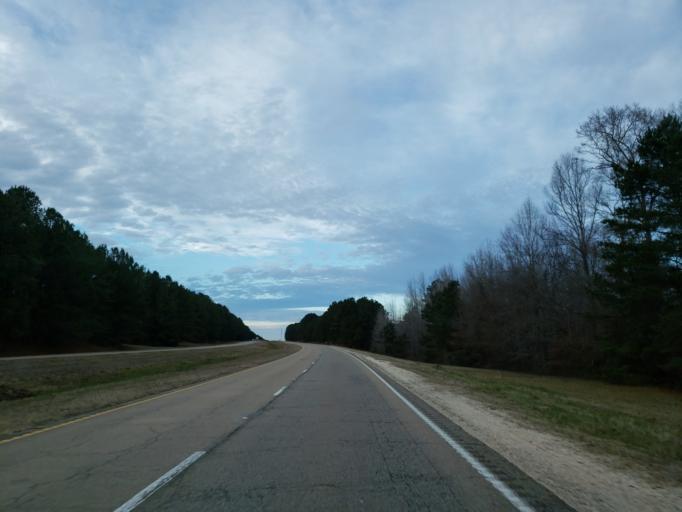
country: US
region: Mississippi
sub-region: Lauderdale County
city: Meridian Station
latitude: 32.6026
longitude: -88.4982
